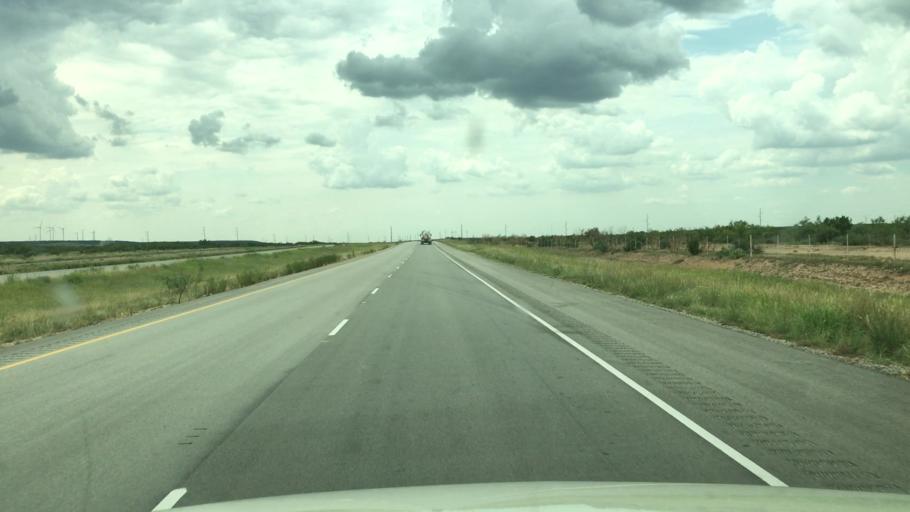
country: US
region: Texas
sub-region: Sterling County
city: Sterling City
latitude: 31.9554
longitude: -101.1956
